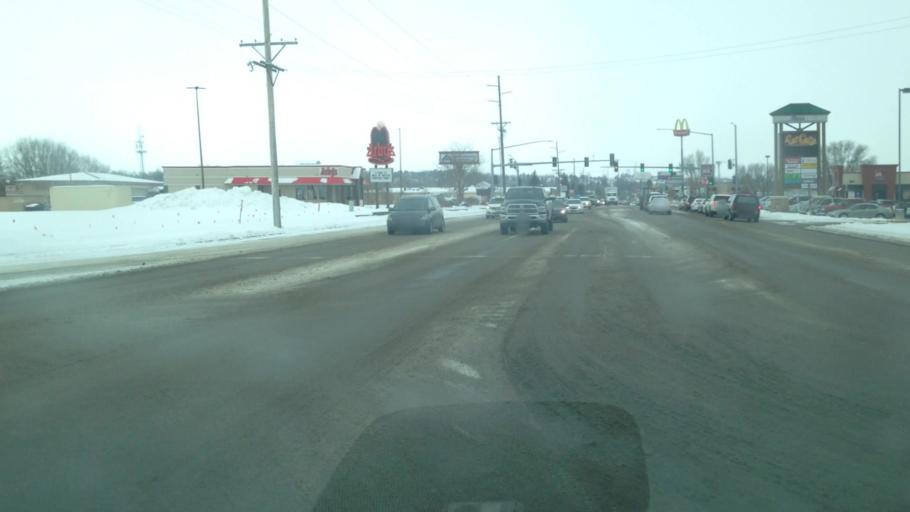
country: US
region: Idaho
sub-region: Madison County
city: Rexburg
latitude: 43.8372
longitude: -111.7781
